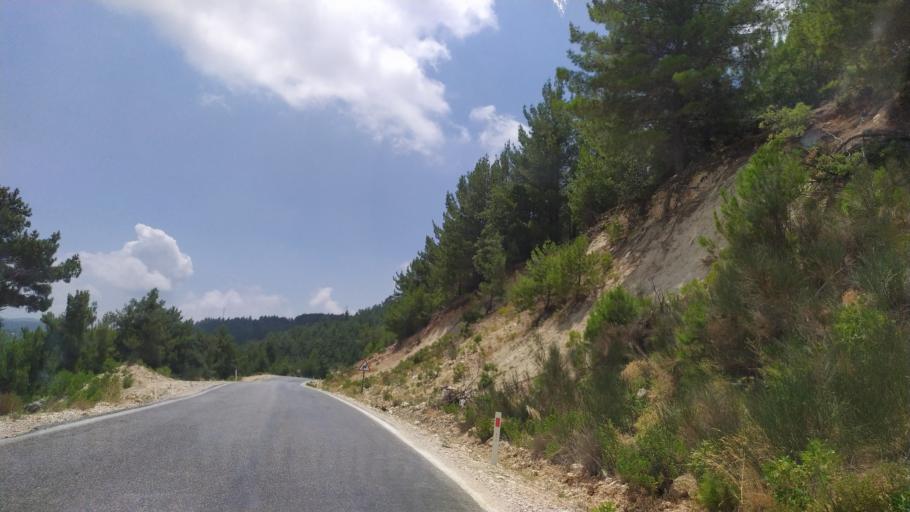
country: TR
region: Mersin
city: Gulnar
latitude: 36.3004
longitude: 33.3804
